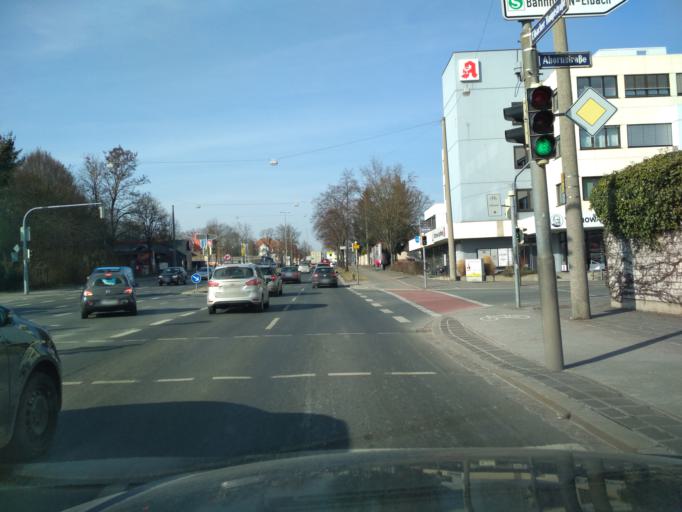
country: DE
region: Bavaria
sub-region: Regierungsbezirk Mittelfranken
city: Stein
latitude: 49.4091
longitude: 11.0352
